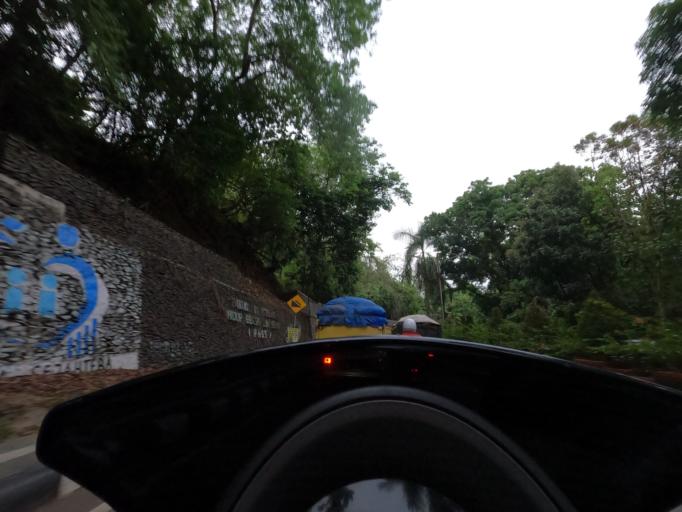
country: ID
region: West Java
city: Lembang
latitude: -6.5795
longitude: 107.7477
